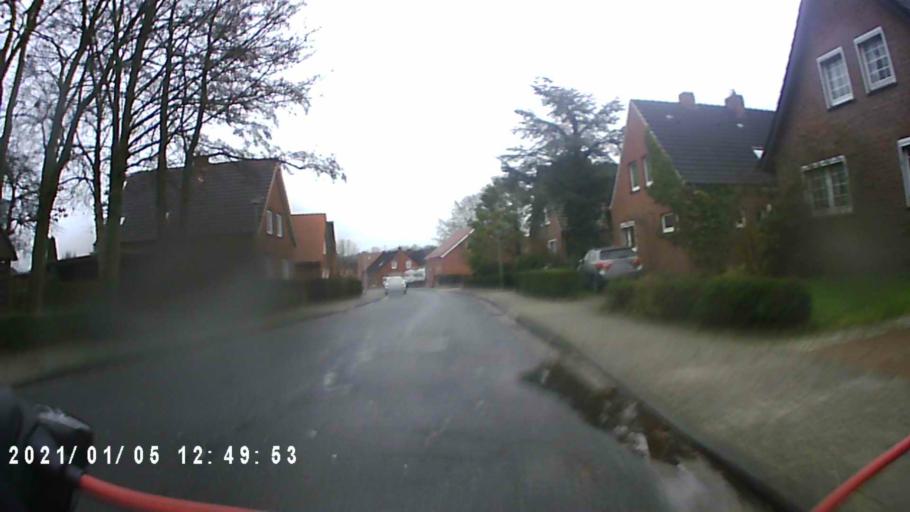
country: DE
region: Lower Saxony
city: Leer
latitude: 53.2351
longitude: 7.4972
